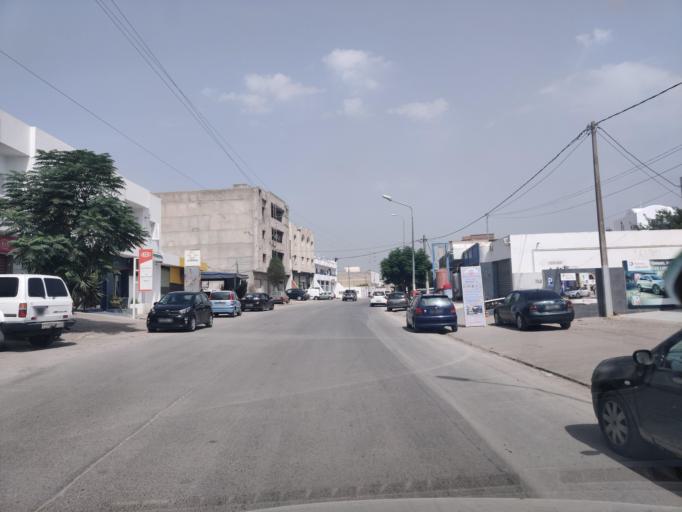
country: TN
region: Nabul
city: Al Hammamat
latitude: 36.4122
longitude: 10.5984
